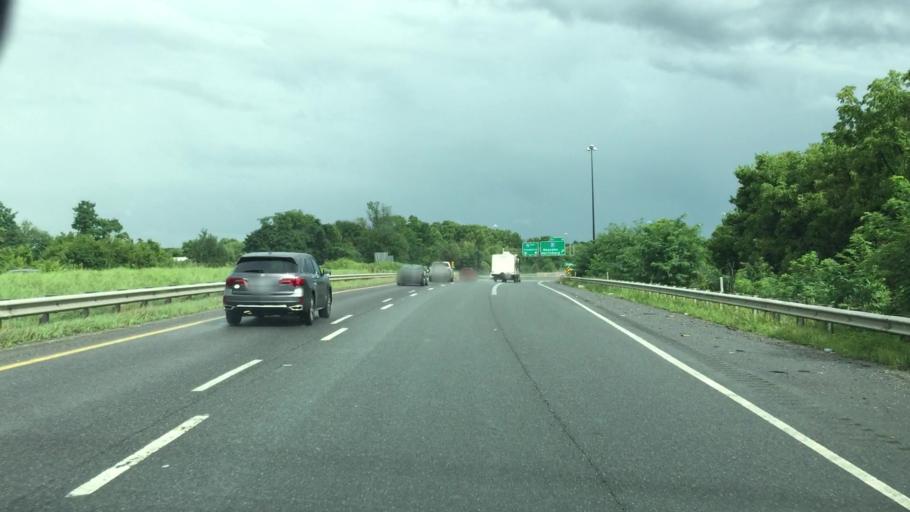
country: US
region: Maryland
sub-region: Washington County
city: Halfway
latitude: 39.6225
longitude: -77.7914
